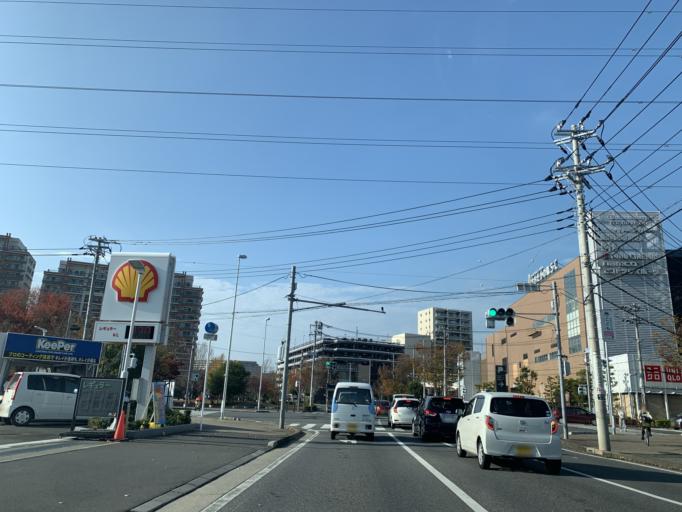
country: JP
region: Chiba
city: Nagareyama
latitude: 35.8688
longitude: 139.9263
